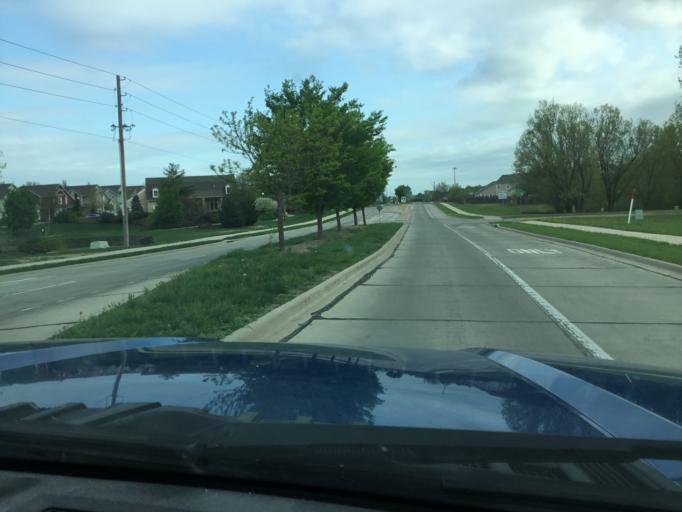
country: US
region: Kansas
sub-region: Douglas County
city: Lawrence
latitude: 38.9867
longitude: -95.2790
